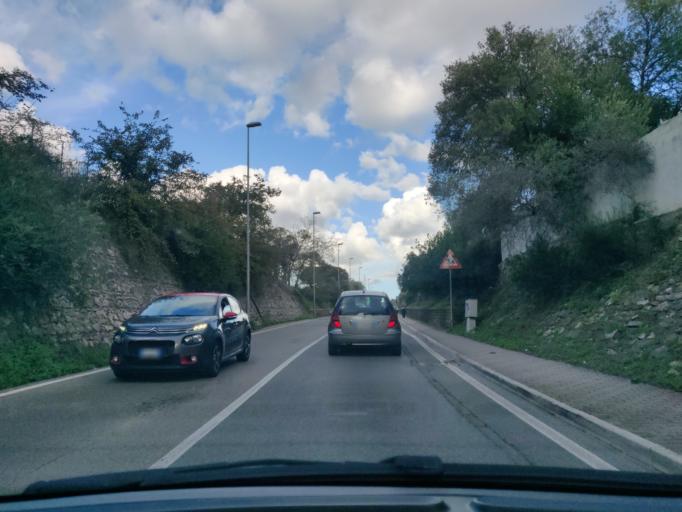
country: IT
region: Latium
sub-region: Citta metropolitana di Roma Capitale
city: Civitavecchia
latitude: 42.1011
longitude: 11.8030
